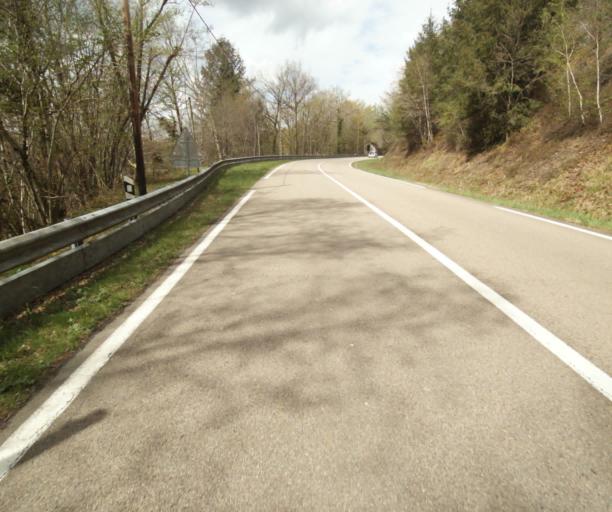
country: FR
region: Limousin
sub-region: Departement de la Correze
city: Sainte-Fortunade
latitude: 45.1968
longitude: 1.8356
